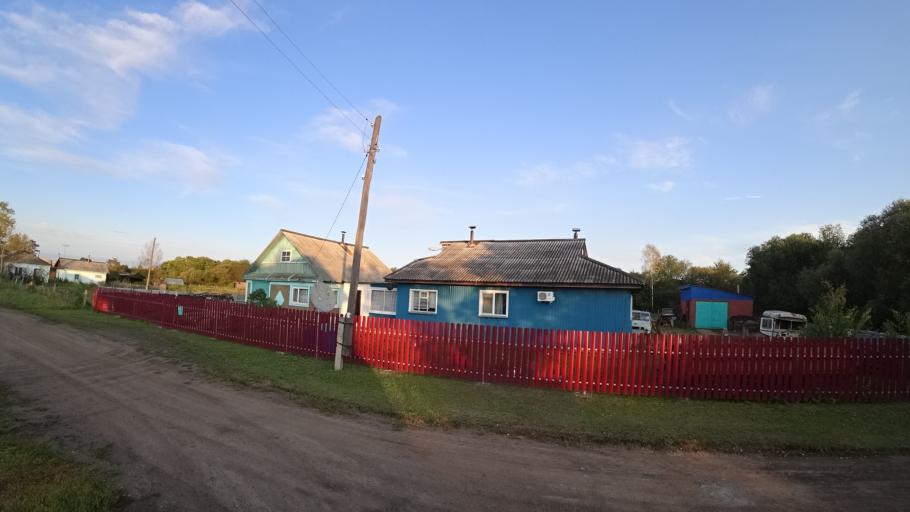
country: RU
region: Amur
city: Arkhara
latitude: 49.3641
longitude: 130.1132
